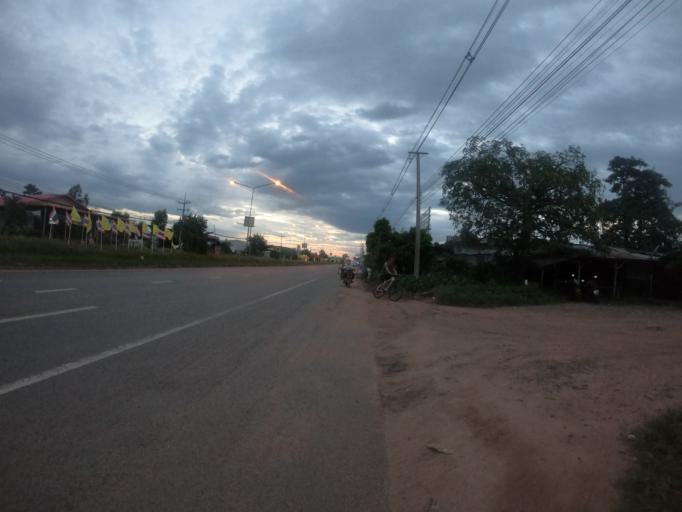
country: TH
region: Surin
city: Kap Choeng
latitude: 14.4524
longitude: 103.6944
